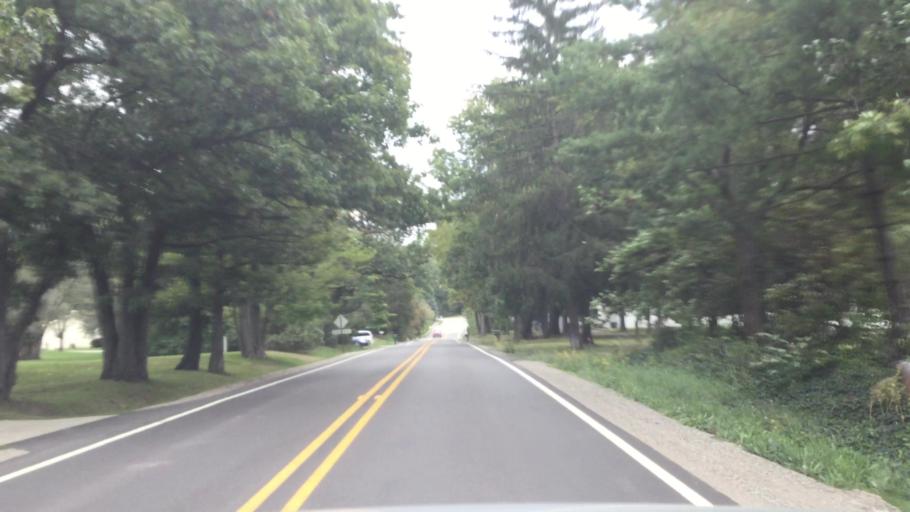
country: US
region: Michigan
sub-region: Livingston County
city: Whitmore Lake
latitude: 42.4664
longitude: -83.8033
